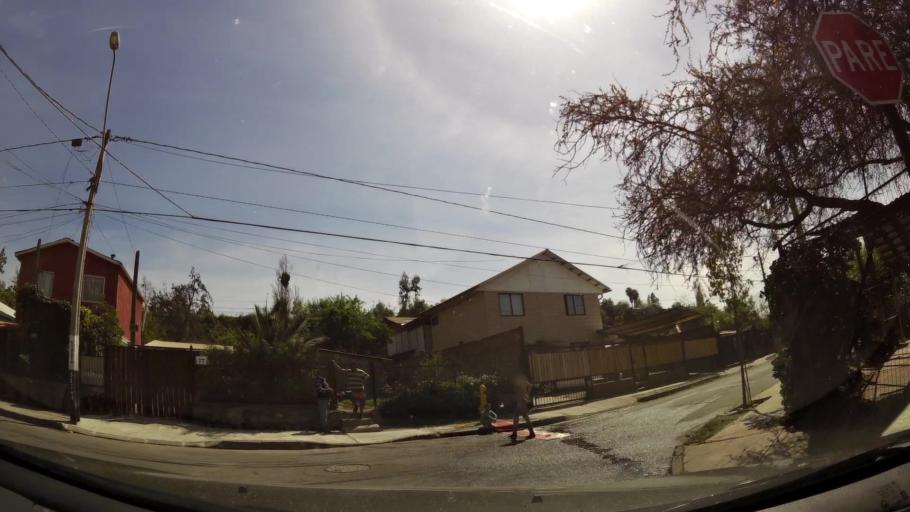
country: CL
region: Santiago Metropolitan
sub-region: Provincia de Cordillera
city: Puente Alto
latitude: -33.6282
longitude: -70.5807
